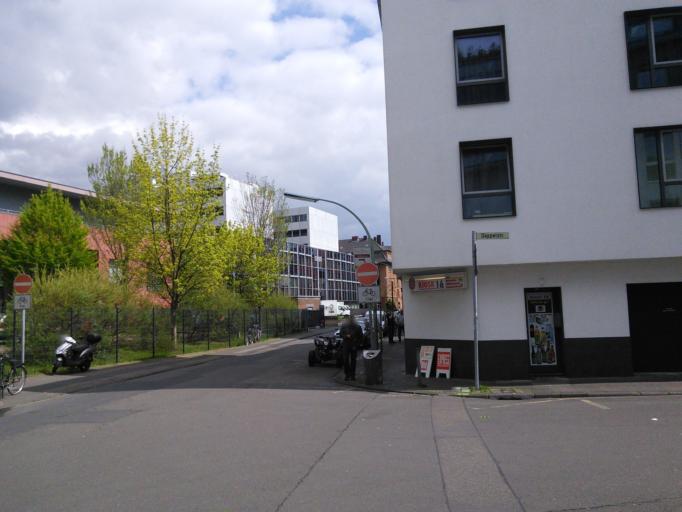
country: DE
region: North Rhine-Westphalia
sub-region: Regierungsbezirk Koln
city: Deutz
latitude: 50.9386
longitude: 6.9733
